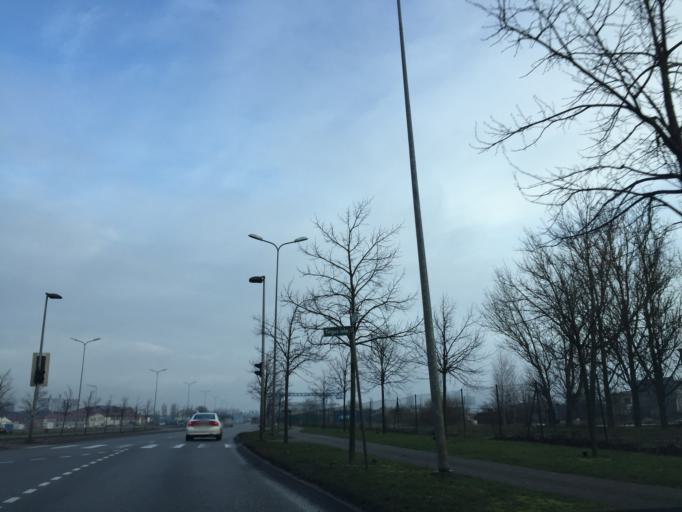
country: LV
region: Liepaja
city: Liepaja
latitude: 56.5164
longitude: 21.0240
